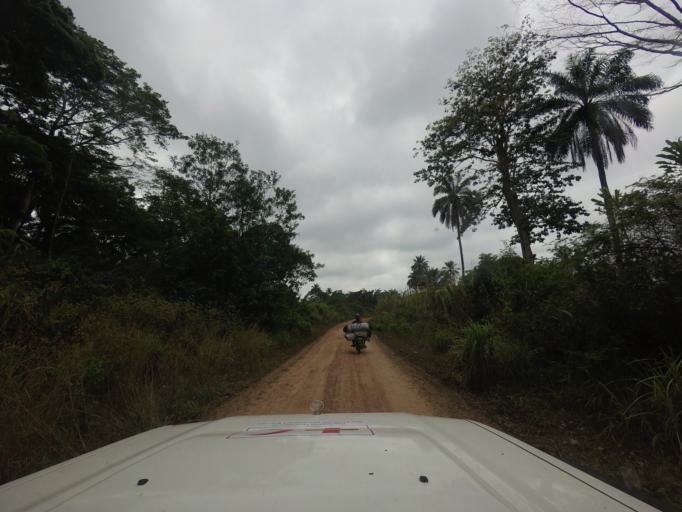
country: LR
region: Lofa
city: Voinjama
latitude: 8.4431
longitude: -9.8085
